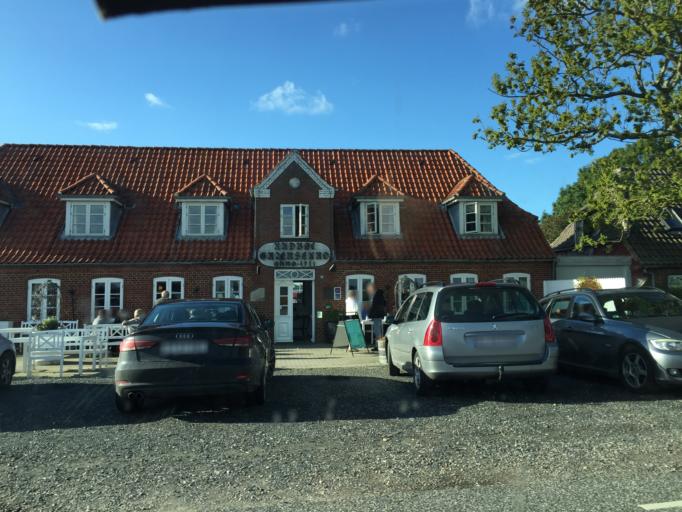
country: DE
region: Schleswig-Holstein
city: Neukirchen
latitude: 54.9001
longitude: 8.7531
